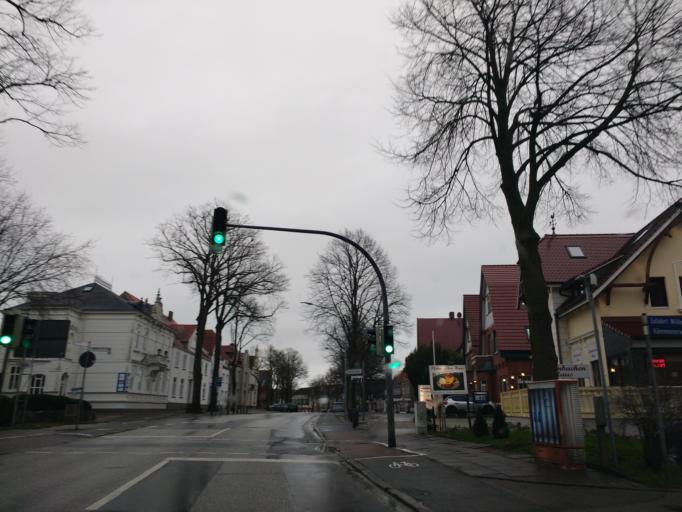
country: DE
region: Schleswig-Holstein
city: Fehmarn
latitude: 54.4410
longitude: 11.1926
